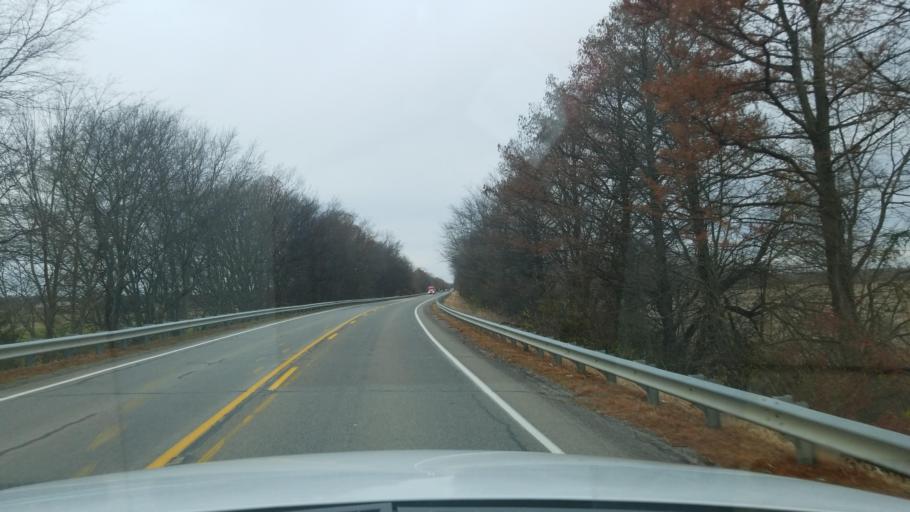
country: US
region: Indiana
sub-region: Posey County
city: Mount Vernon
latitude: 37.9307
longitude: -88.0020
